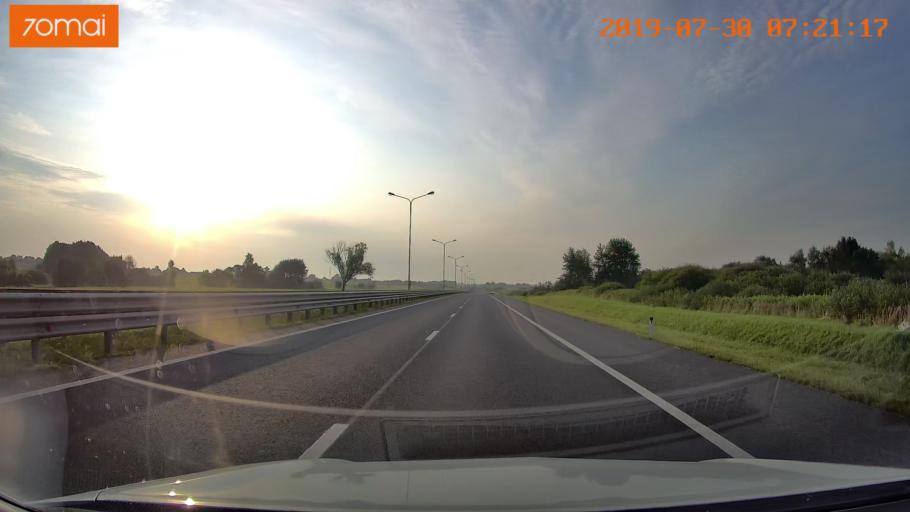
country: RU
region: Kaliningrad
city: Bol'shoe Isakovo
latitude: 54.6970
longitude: 20.7249
